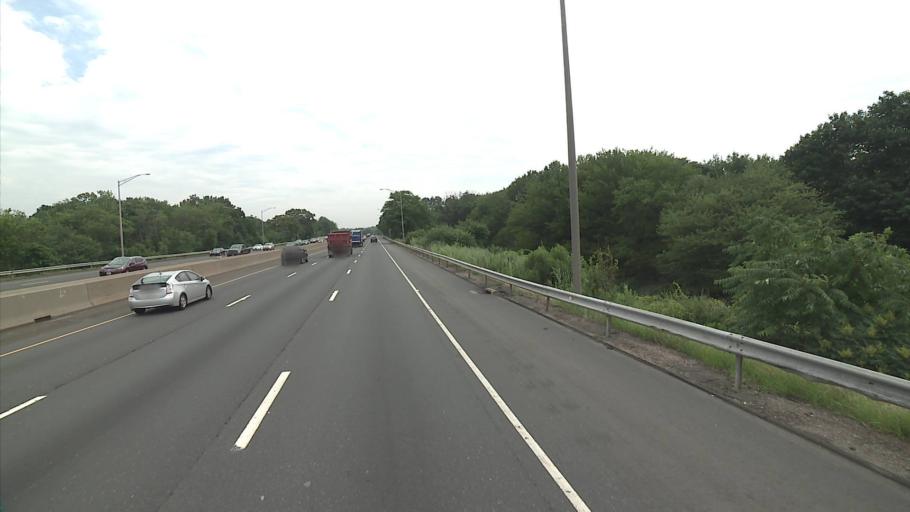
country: US
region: Connecticut
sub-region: Fairfield County
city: Southport
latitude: 41.1317
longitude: -73.2964
